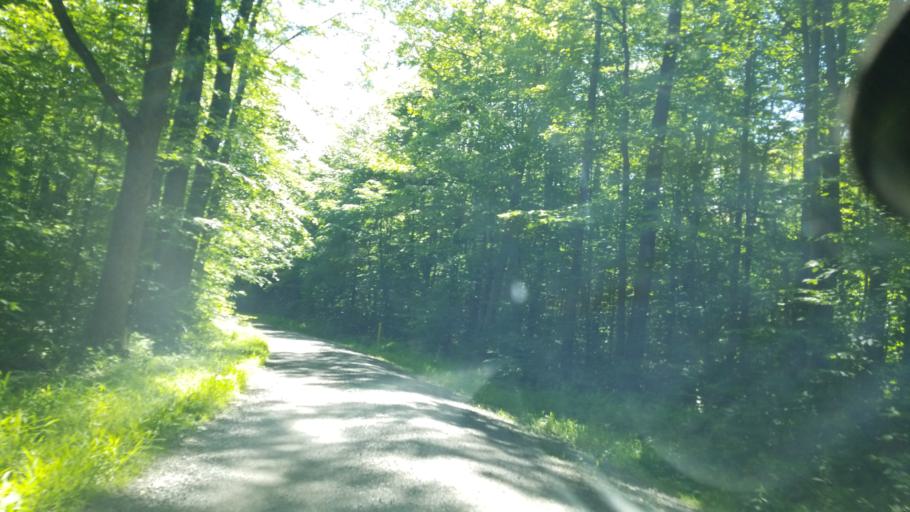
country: US
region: Pennsylvania
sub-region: Clearfield County
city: Clearfield
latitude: 41.2093
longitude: -78.4049
